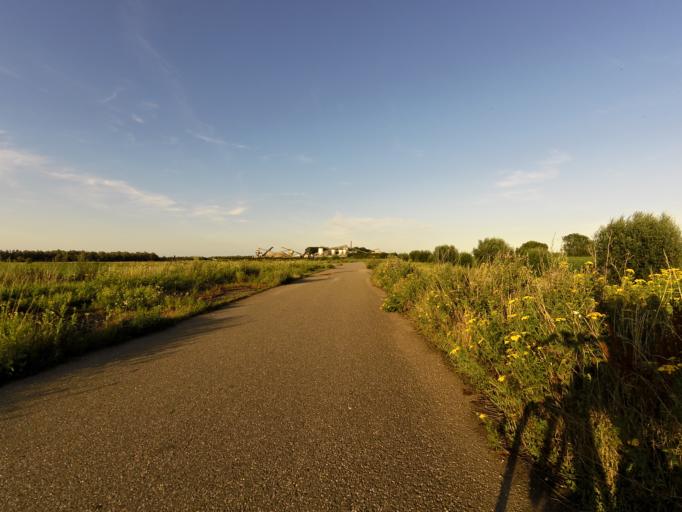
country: NL
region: Gelderland
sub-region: Gemeente Groesbeek
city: Berg en Dal
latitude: 51.8747
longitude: 5.8995
